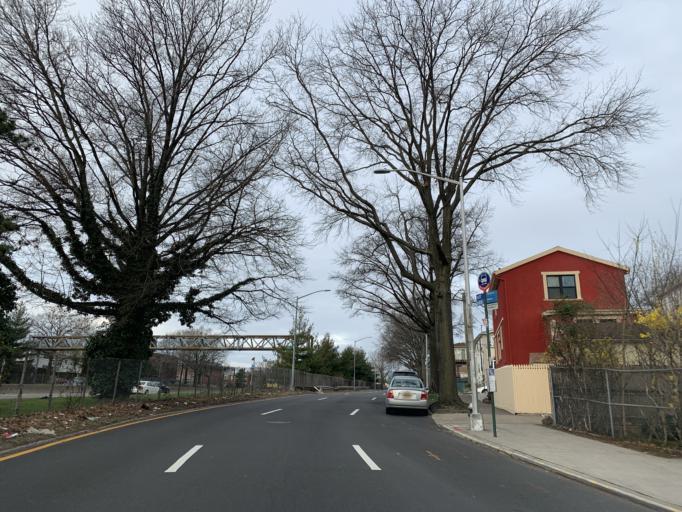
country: US
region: New York
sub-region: Queens County
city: Jamaica
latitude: 40.7386
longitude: -73.7966
